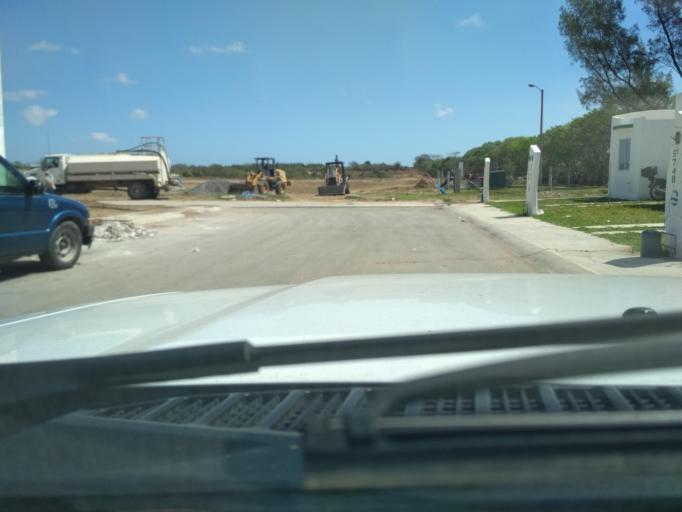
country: MX
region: Veracruz
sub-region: Veracruz
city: Las Amapolas
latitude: 19.1321
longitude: -96.2042
